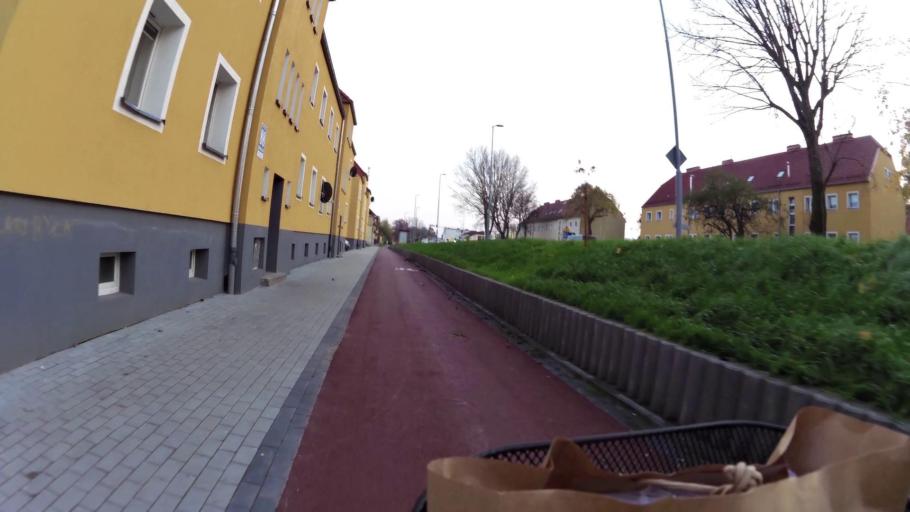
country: PL
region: West Pomeranian Voivodeship
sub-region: Koszalin
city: Koszalin
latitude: 54.2044
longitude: 16.1584
